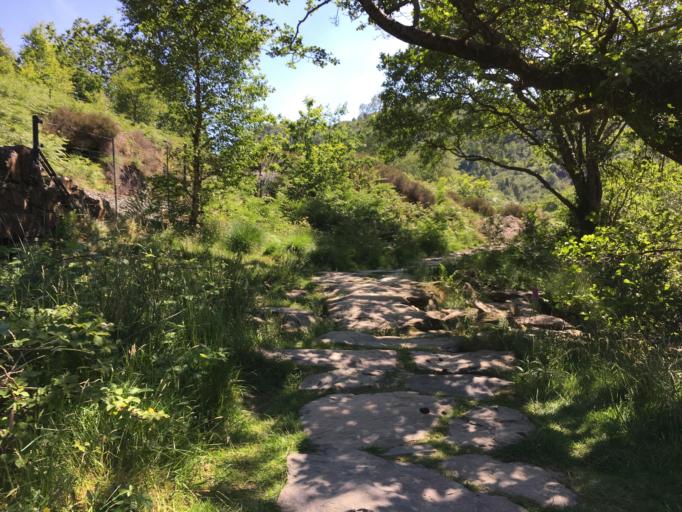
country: GB
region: Wales
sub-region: Gwynedd
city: Penrhyndeudraeth
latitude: 53.0042
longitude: -4.0992
